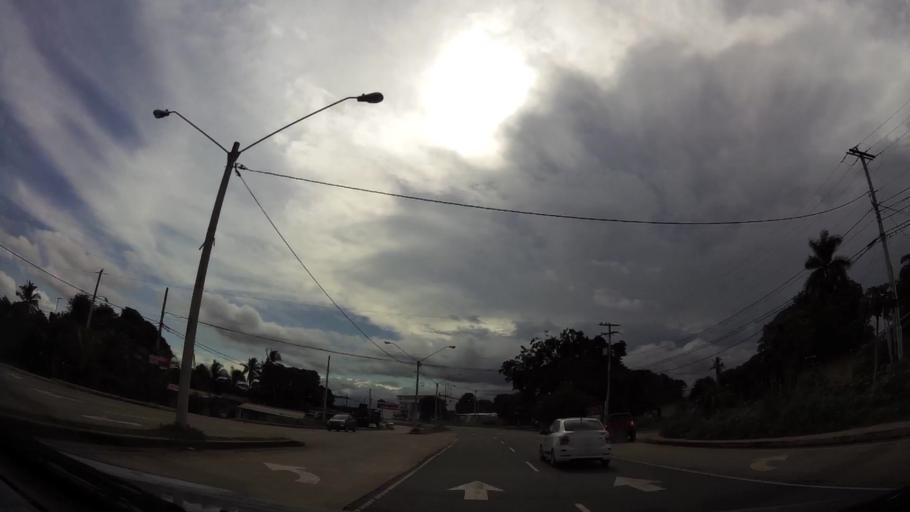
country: PA
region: Panama
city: Guadalupe
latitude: 8.8617
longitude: -79.8074
